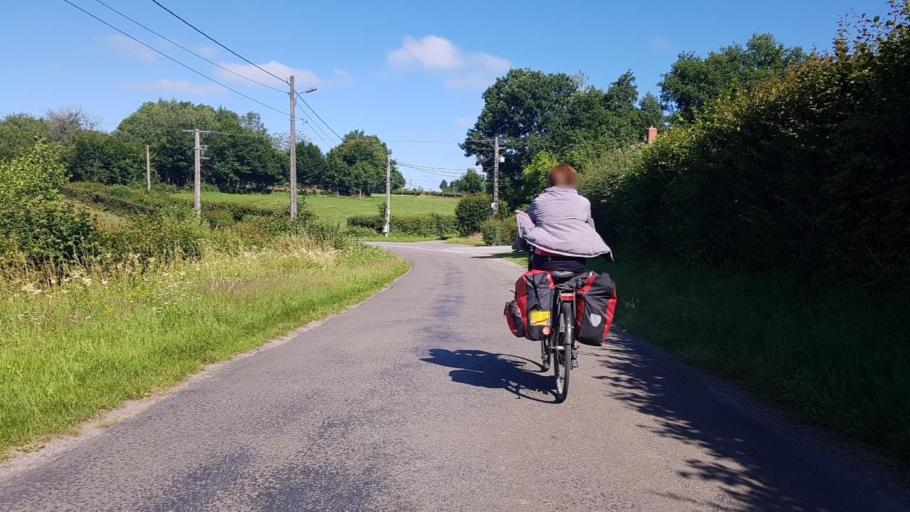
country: FR
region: Nord-Pas-de-Calais
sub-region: Departement du Nord
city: Anor
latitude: 49.9842
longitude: 4.1262
